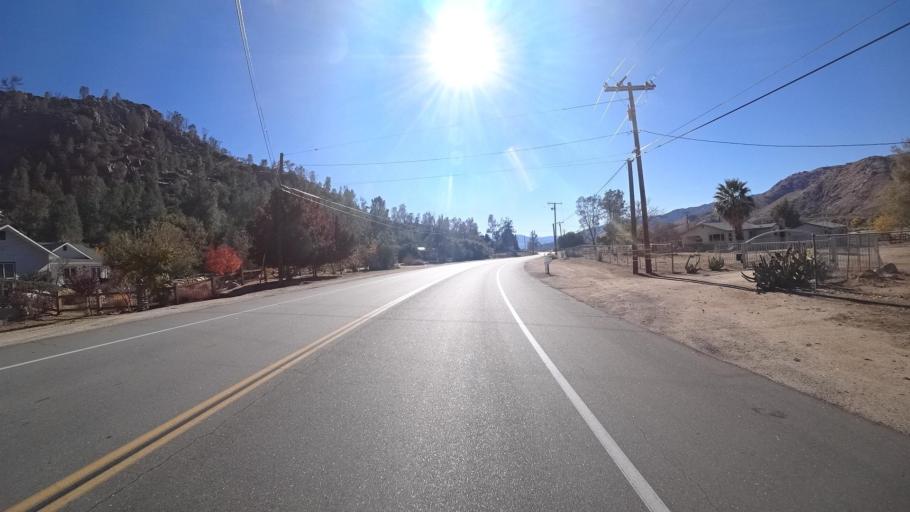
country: US
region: California
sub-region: Kern County
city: Kernville
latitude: 35.7347
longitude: -118.4142
